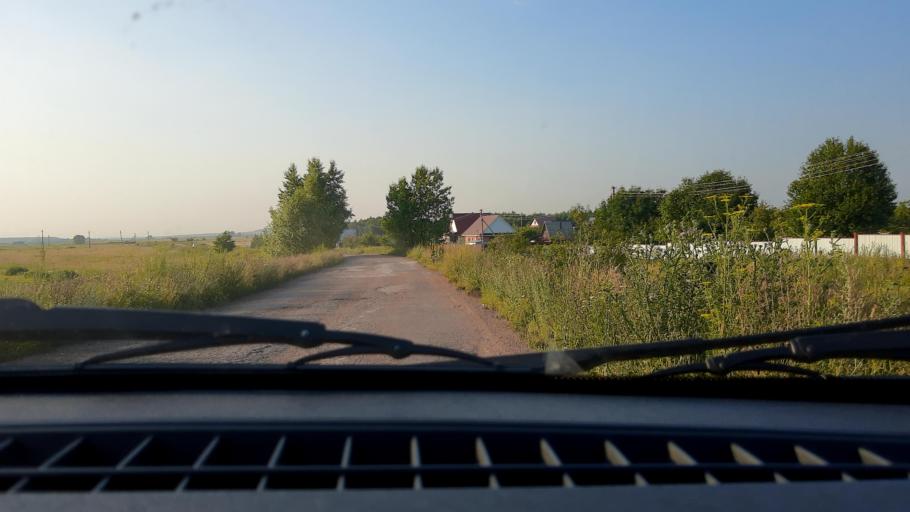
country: RU
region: Bashkortostan
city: Asanovo
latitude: 54.9152
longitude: 55.6273
